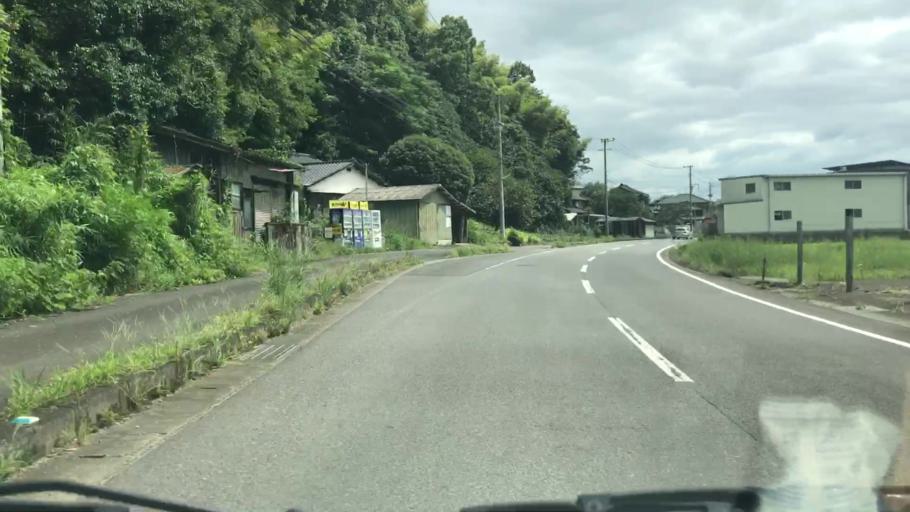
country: JP
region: Saga Prefecture
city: Takeocho-takeo
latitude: 33.2294
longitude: 130.1527
